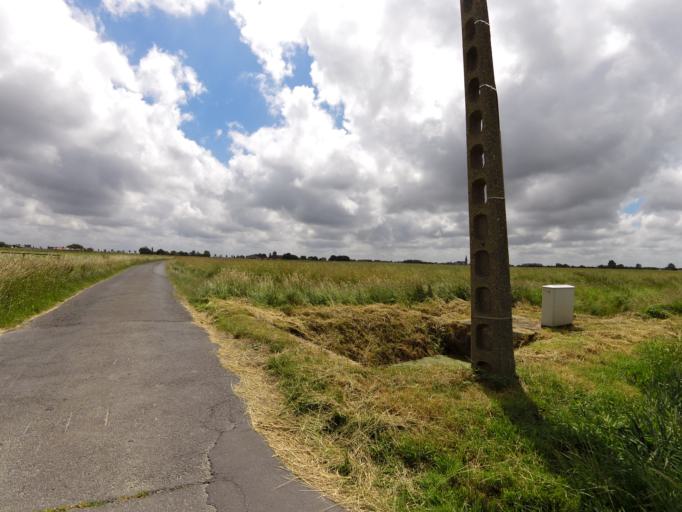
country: BE
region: Flanders
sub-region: Provincie West-Vlaanderen
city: Gistel
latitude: 51.1454
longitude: 2.9259
